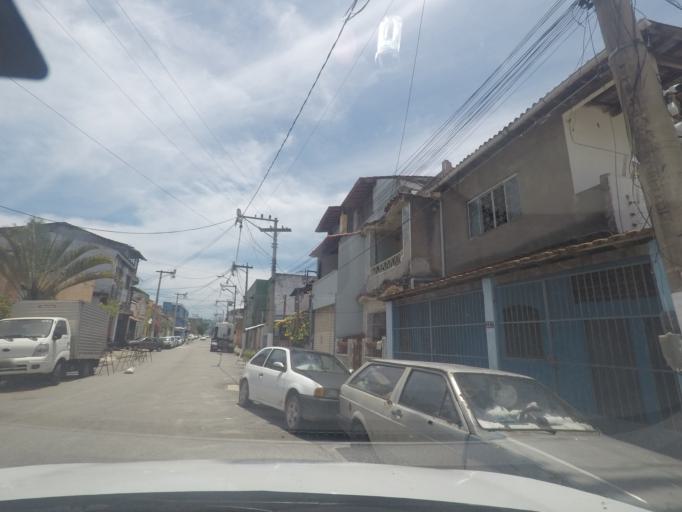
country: BR
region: Rio de Janeiro
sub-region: Niteroi
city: Niteroi
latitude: -22.8706
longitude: -43.1012
